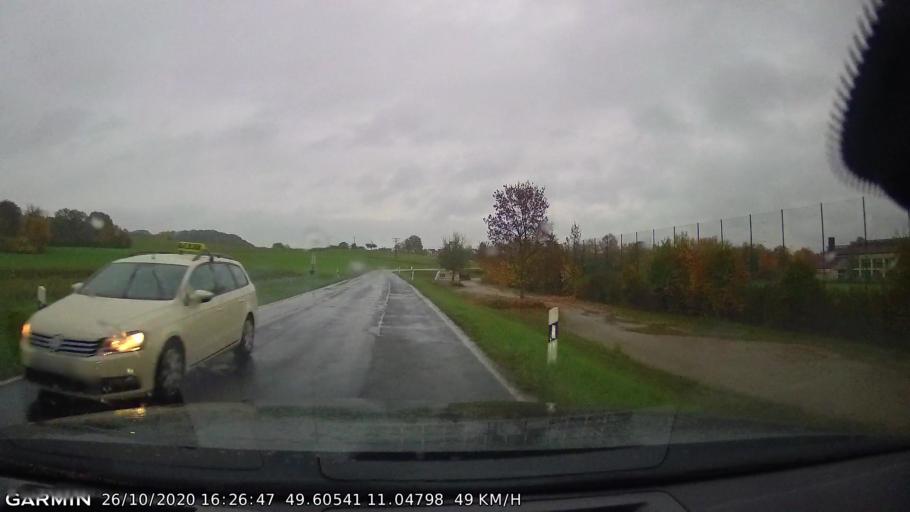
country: DE
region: Bavaria
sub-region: Regierungsbezirk Mittelfranken
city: Spardorf
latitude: 49.6054
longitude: 11.0482
